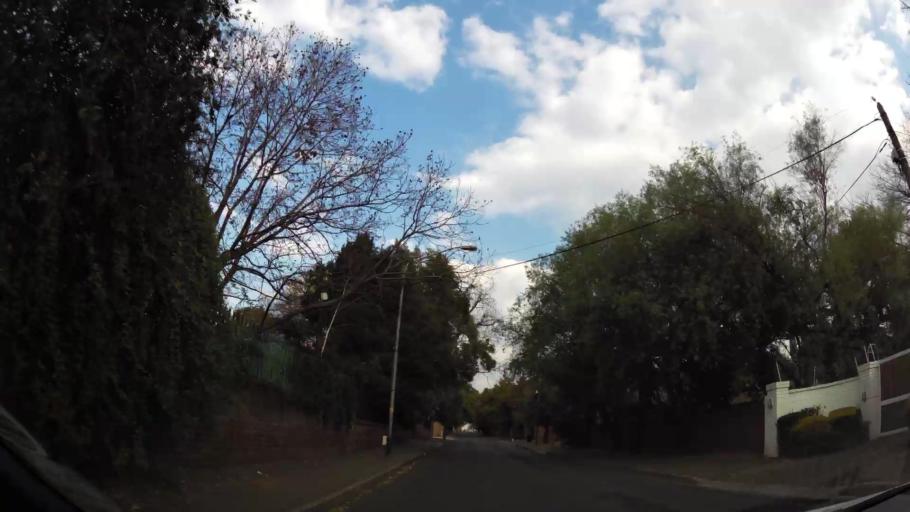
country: ZA
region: Gauteng
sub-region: Ekurhuleni Metropolitan Municipality
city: Germiston
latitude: -26.2362
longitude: 28.1679
